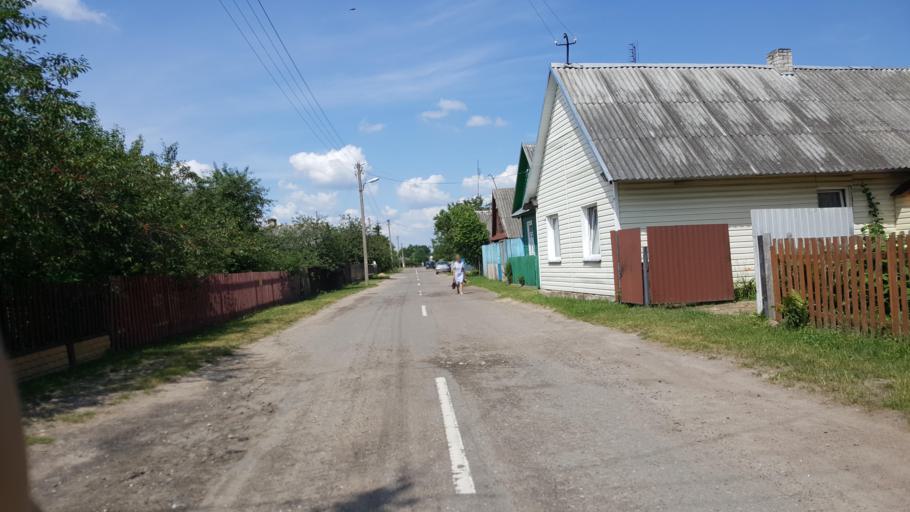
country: BY
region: Brest
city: Kamyanyets
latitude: 52.4000
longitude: 23.8169
